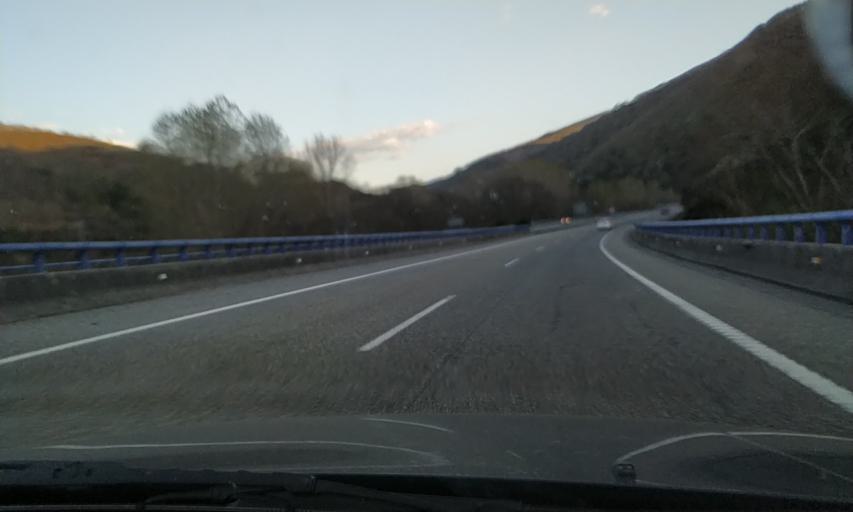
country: ES
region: Castille and Leon
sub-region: Provincia de Leon
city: Trabadelo
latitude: 42.6535
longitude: -6.8918
